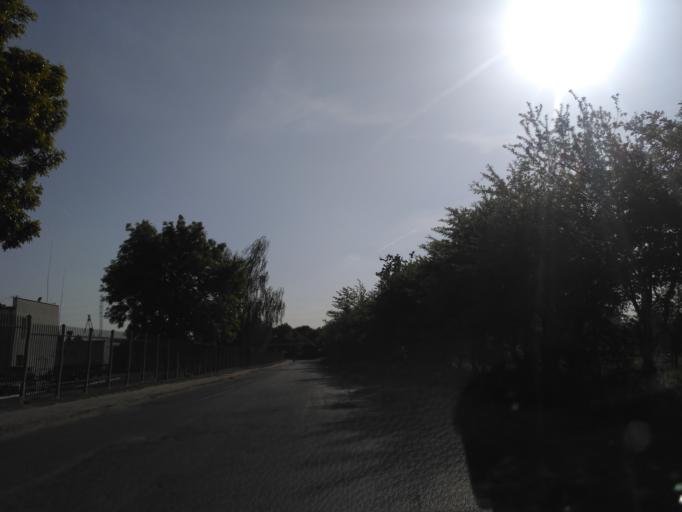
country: PL
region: Lublin Voivodeship
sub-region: Powiat lubelski
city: Lublin
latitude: 51.2138
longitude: 22.5601
